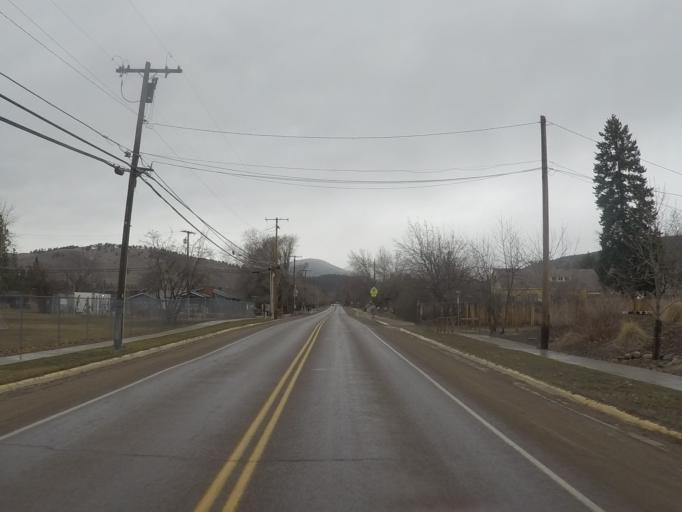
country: US
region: Montana
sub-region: Missoula County
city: East Missoula
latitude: 46.8916
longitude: -113.9656
